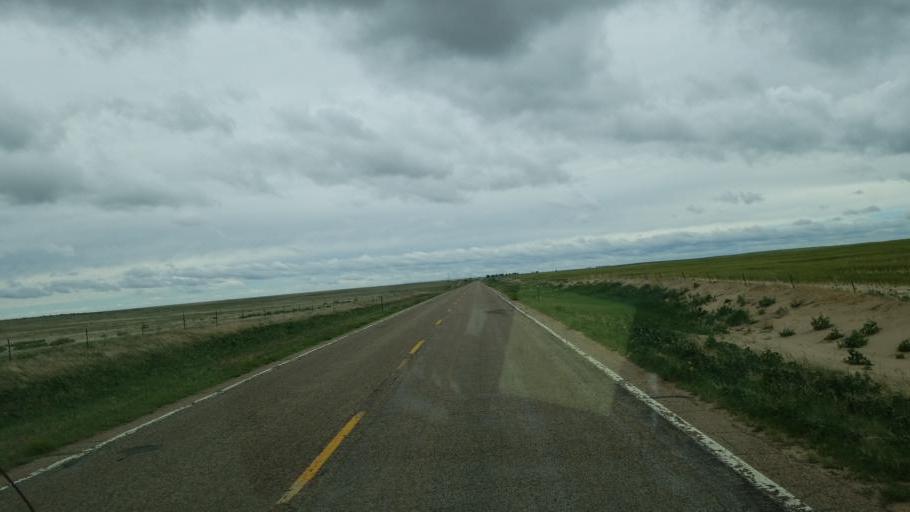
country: US
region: Colorado
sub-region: Lincoln County
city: Hugo
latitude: 38.8518
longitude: -103.6690
